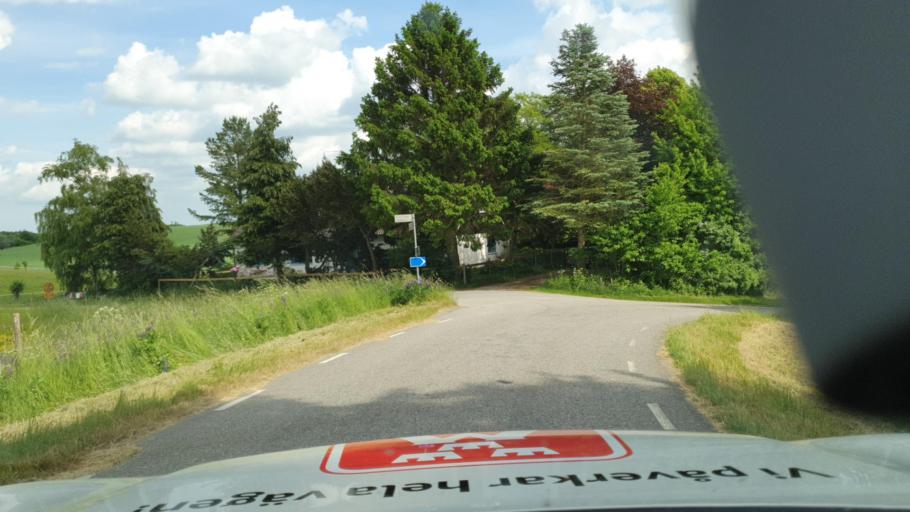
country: SE
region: Skane
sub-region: Skurups Kommun
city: Skurup
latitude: 55.5243
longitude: 13.4544
